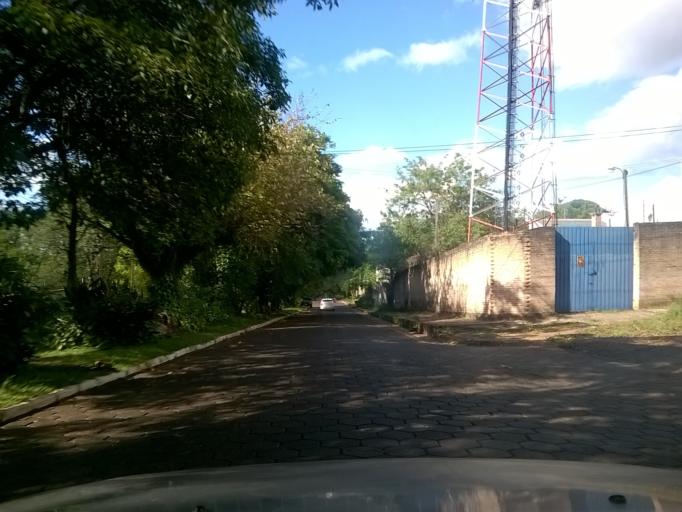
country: PY
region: Alto Parana
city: Presidente Franco
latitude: -25.5304
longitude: -54.6288
